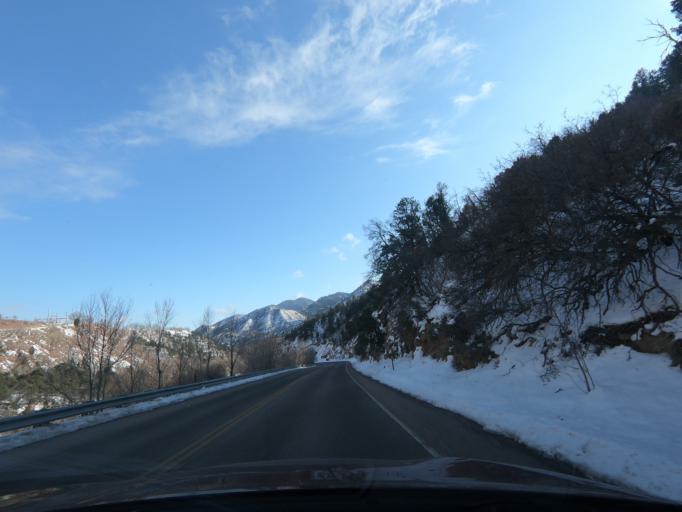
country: US
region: Colorado
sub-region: El Paso County
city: Manitou Springs
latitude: 38.8673
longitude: -104.9248
